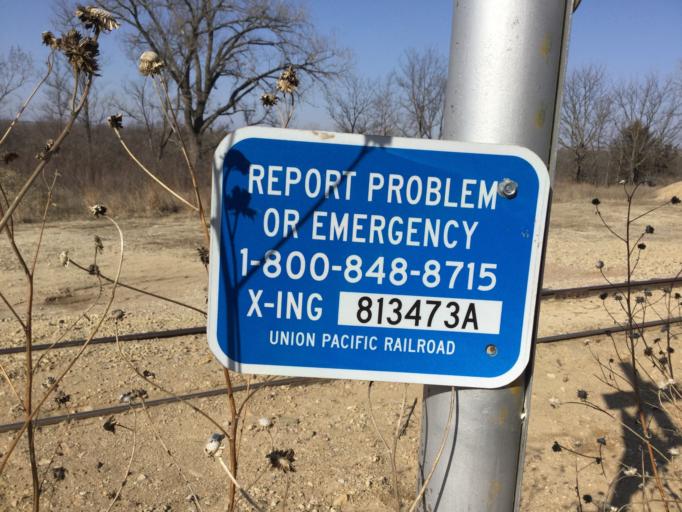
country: US
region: Kansas
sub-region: Marshall County
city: Blue Rapids
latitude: 39.7604
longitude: -96.6781
